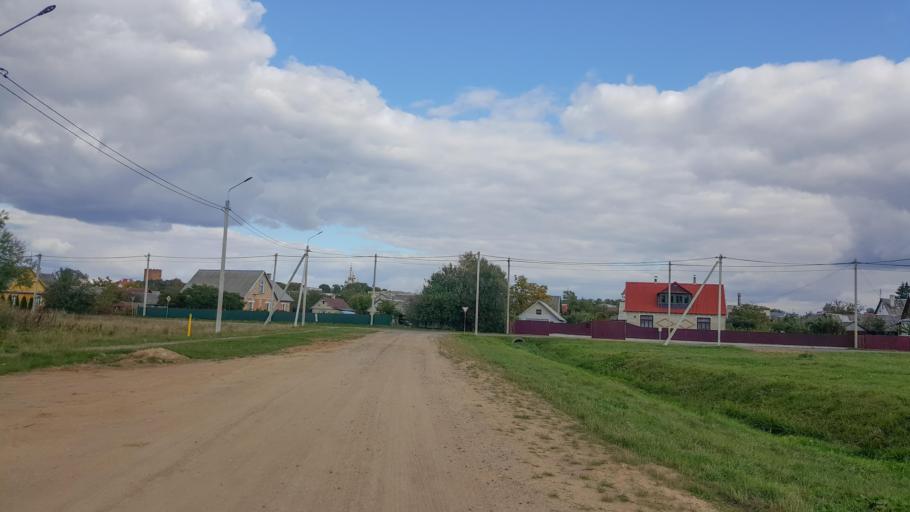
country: BY
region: Brest
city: Kamyanyets
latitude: 52.4014
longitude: 23.8119
